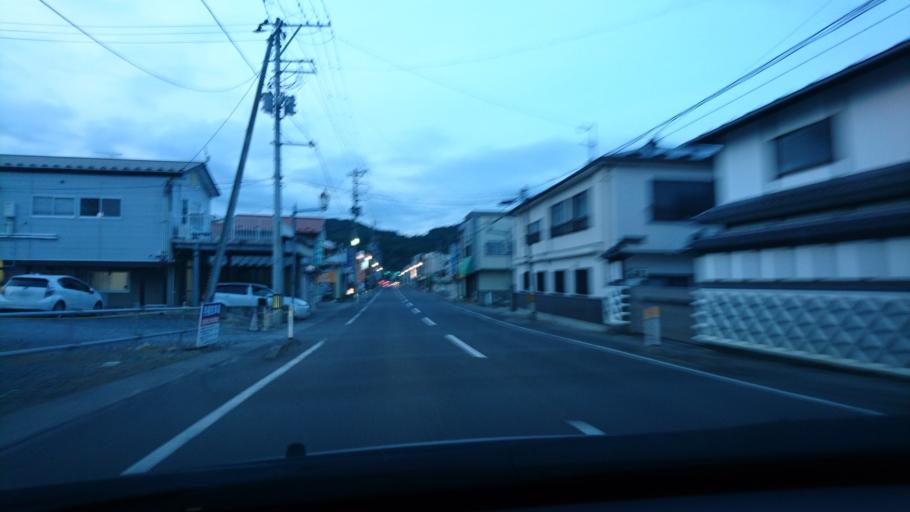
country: JP
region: Iwate
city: Ichinoseki
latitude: 38.8287
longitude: 140.9863
